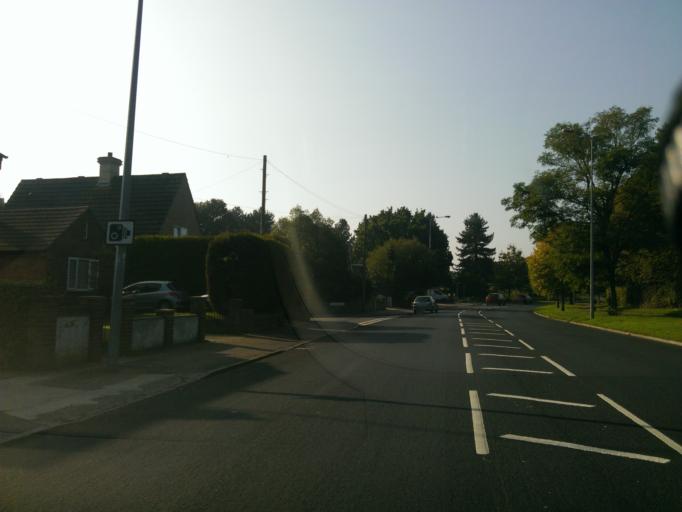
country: GB
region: England
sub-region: Essex
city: Colchester
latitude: 51.8732
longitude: 0.8804
